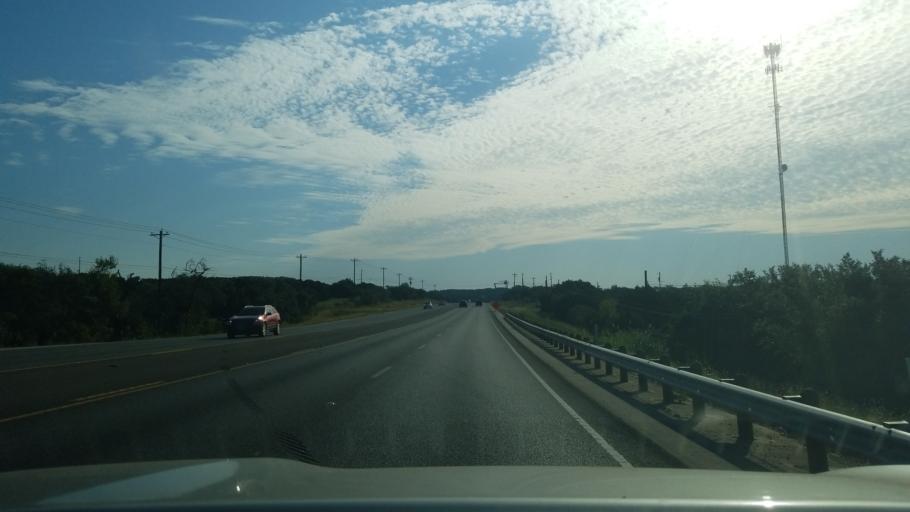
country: US
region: Texas
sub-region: Hays County
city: Dripping Springs
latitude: 30.1946
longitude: -98.0587
